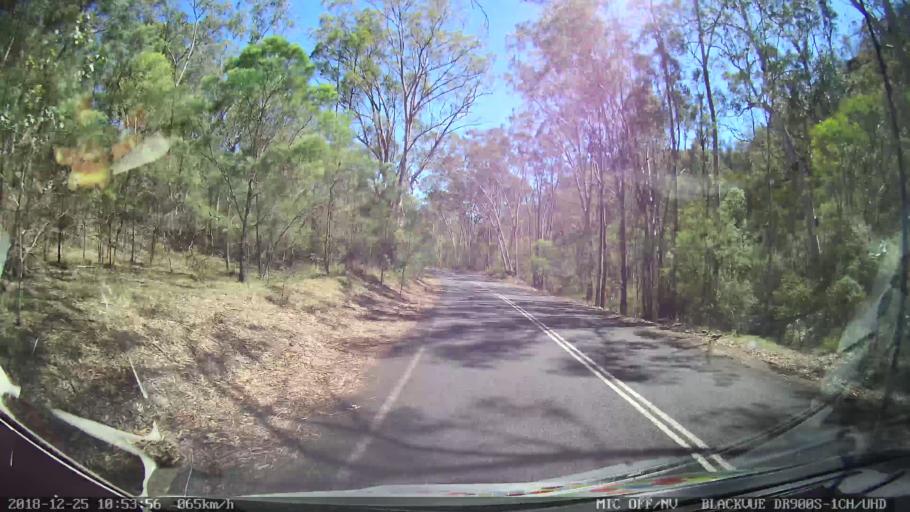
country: AU
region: New South Wales
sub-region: Upper Hunter Shire
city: Merriwa
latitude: -32.4151
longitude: 150.2730
